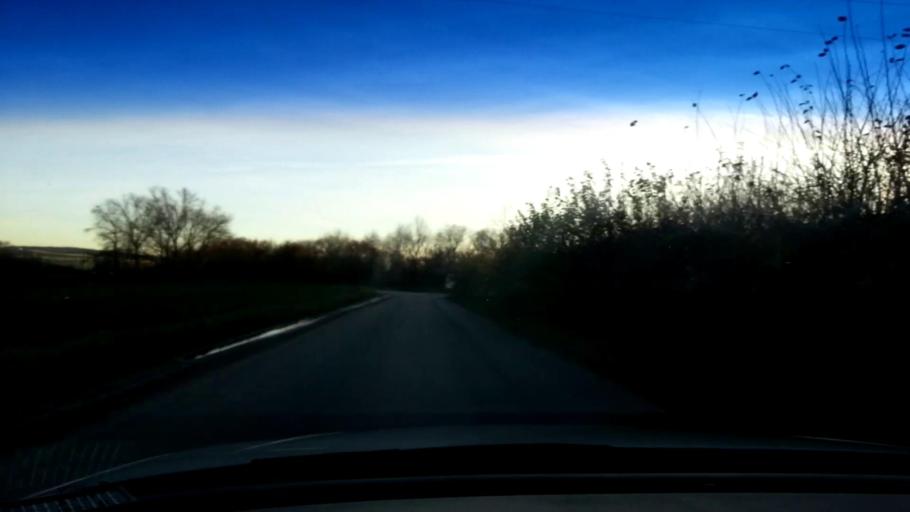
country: DE
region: Bavaria
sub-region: Upper Franconia
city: Ebensfeld
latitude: 50.0591
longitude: 10.9485
